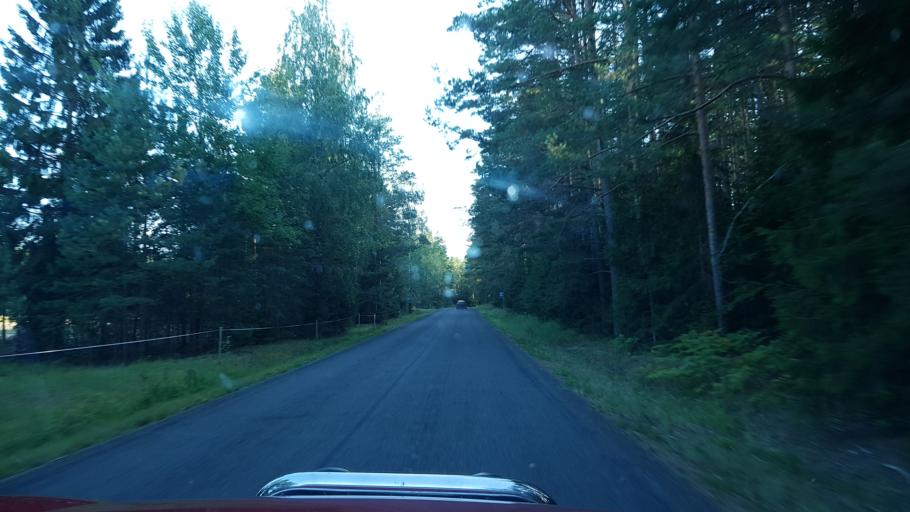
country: EE
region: Paernumaa
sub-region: Paikuse vald
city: Paikuse
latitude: 58.1194
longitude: 24.5532
